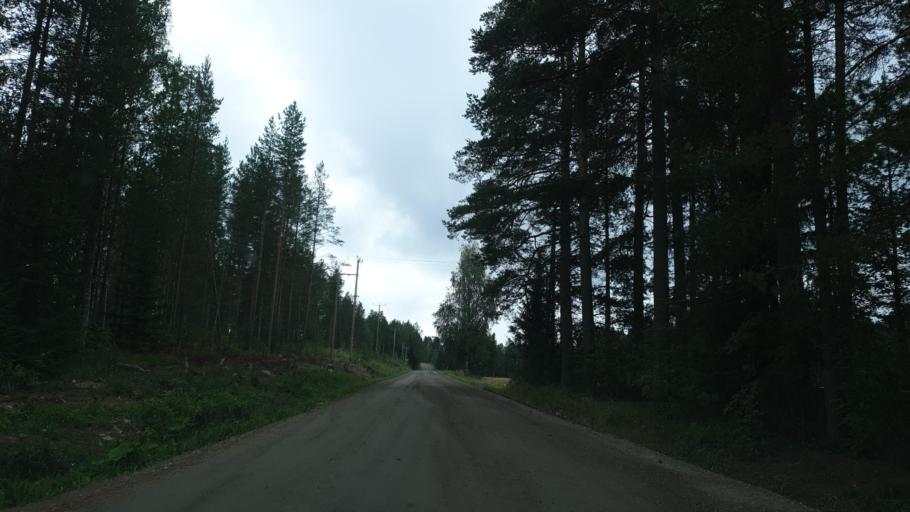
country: FI
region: Northern Savo
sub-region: Kuopio
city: Nilsiae
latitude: 63.1997
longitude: 28.2392
